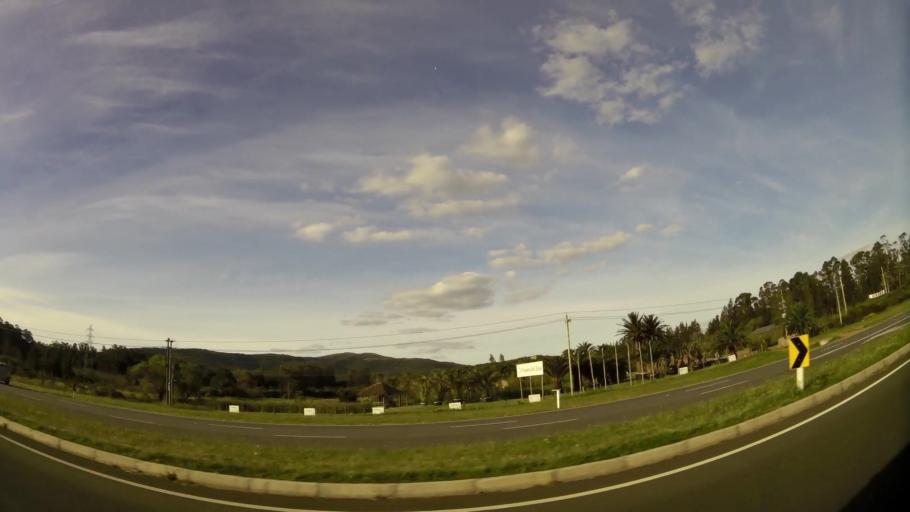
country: UY
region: Maldonado
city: Pan de Azucar
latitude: -34.7876
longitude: -55.3260
